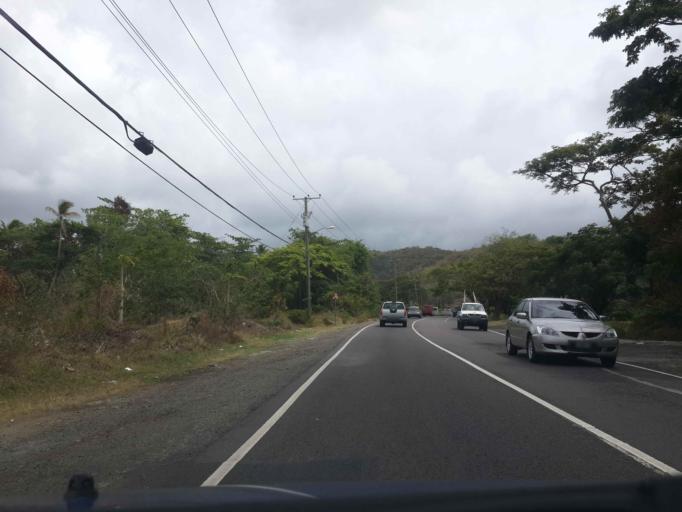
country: LC
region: Castries Quarter
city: Bisee
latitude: 14.0366
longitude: -60.9689
